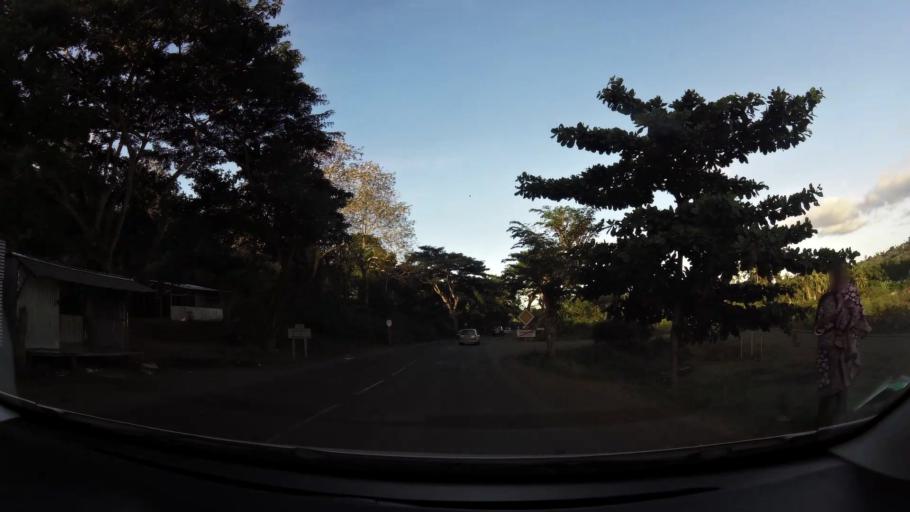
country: YT
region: Dembeni
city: Dembeni
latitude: -12.8370
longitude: 45.1780
